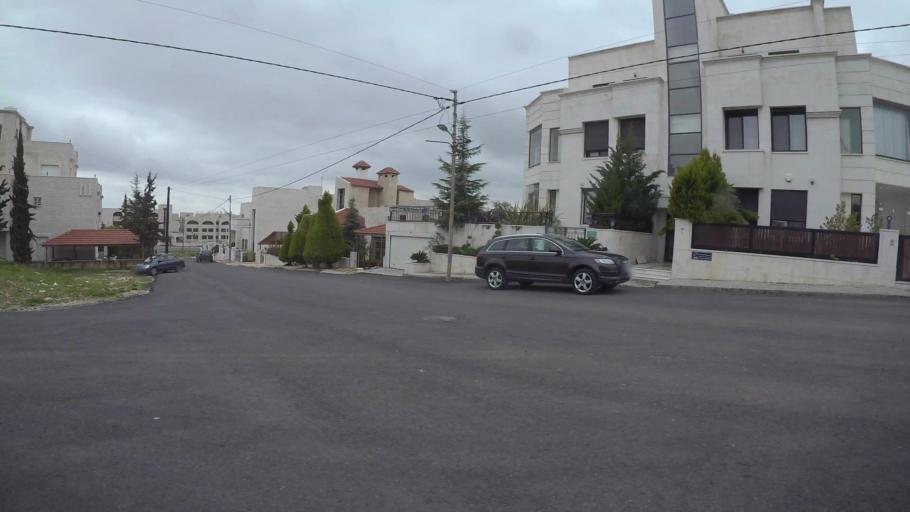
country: JO
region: Amman
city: Al Jubayhah
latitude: 31.9905
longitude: 35.8419
